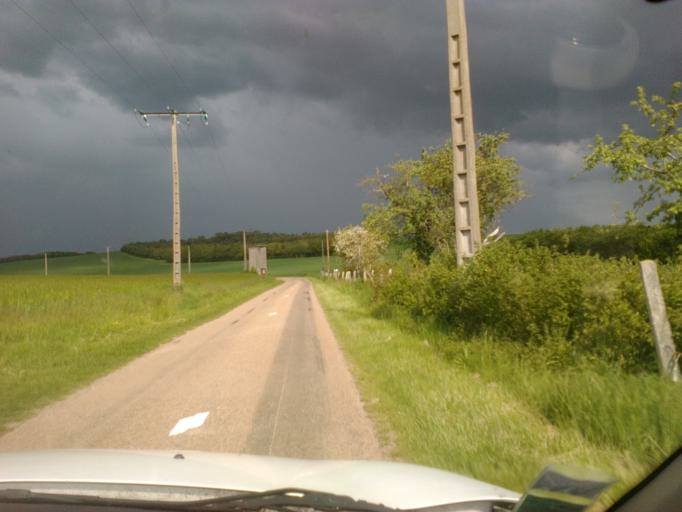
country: FR
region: Champagne-Ardenne
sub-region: Departement de l'Aube
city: Nogent-sur-Seine
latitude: 48.3798
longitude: 3.5067
